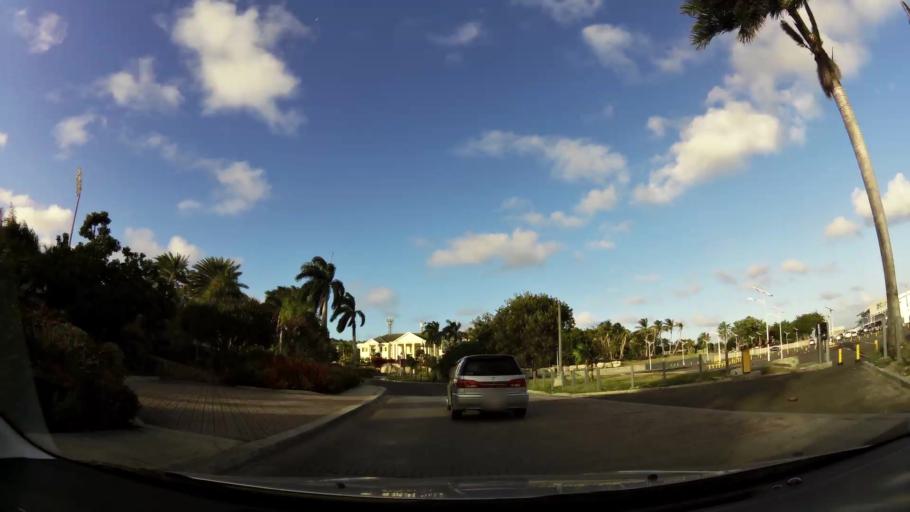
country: AG
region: Saint George
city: Piggotts
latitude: 17.1408
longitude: -61.7937
